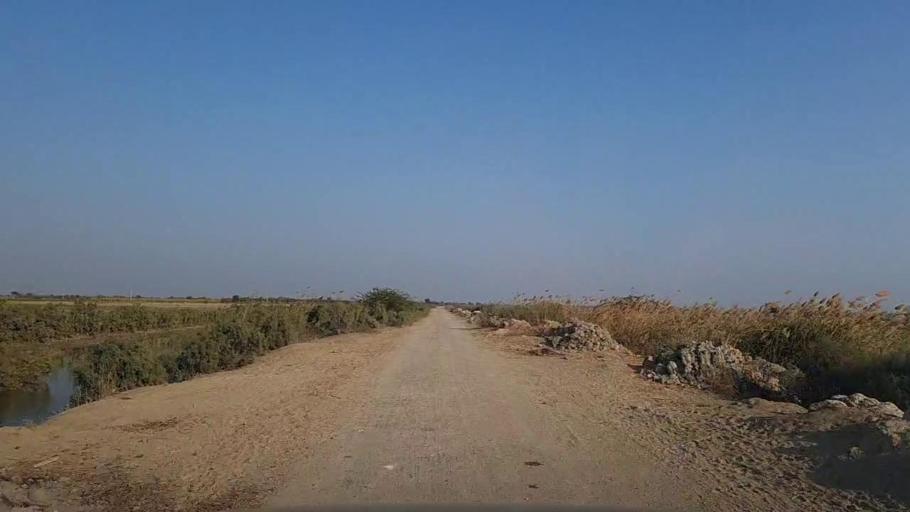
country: PK
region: Sindh
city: Tando Mittha Khan
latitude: 25.9252
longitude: 69.0799
